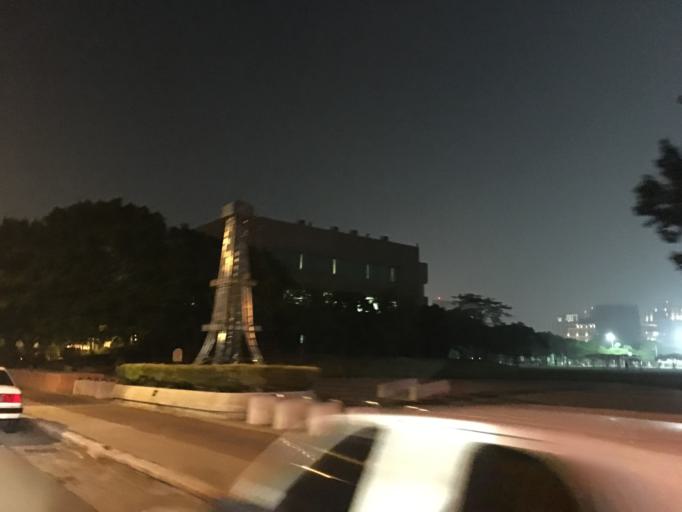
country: TW
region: Taiwan
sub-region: Miaoli
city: Miaoli
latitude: 24.6885
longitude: 120.8856
